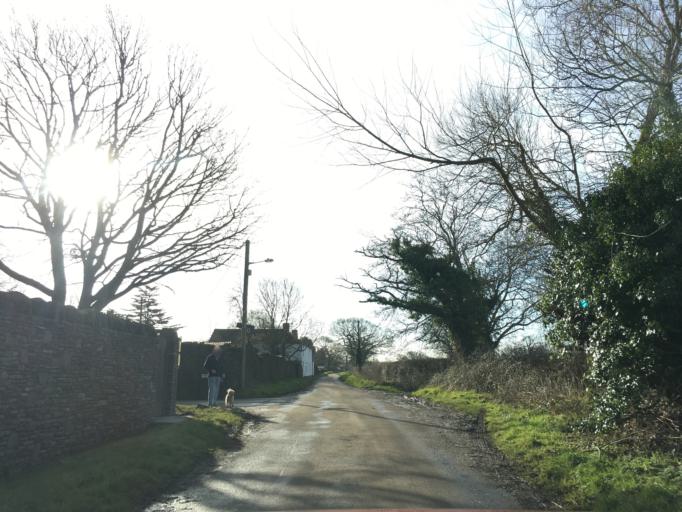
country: GB
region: England
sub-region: South Gloucestershire
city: Yate
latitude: 51.5520
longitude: -2.4432
